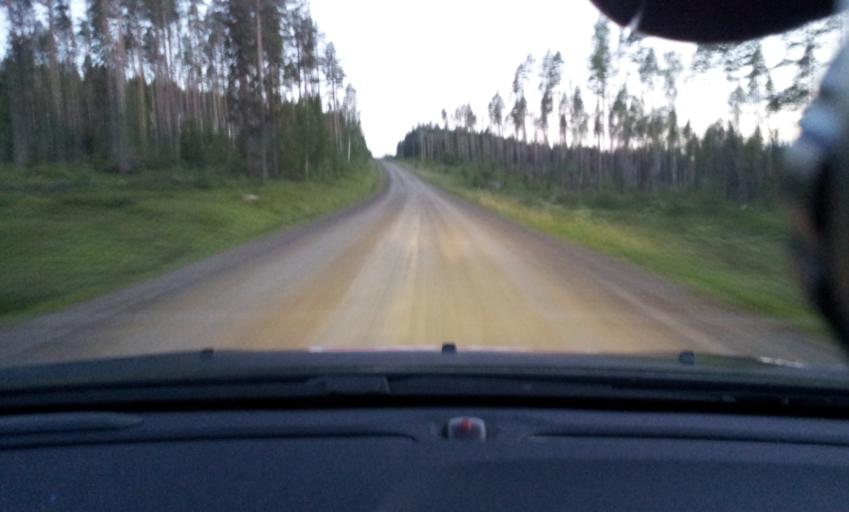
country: SE
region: Vaesternorrland
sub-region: Ange Kommun
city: Ange
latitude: 62.7630
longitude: 15.7034
